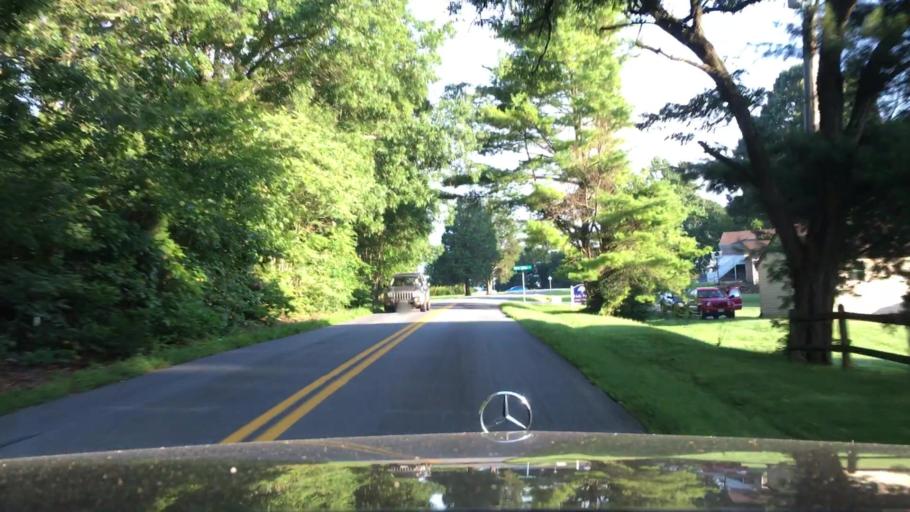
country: US
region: Virginia
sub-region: Campbell County
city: Timberlake
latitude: 37.2952
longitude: -79.2811
